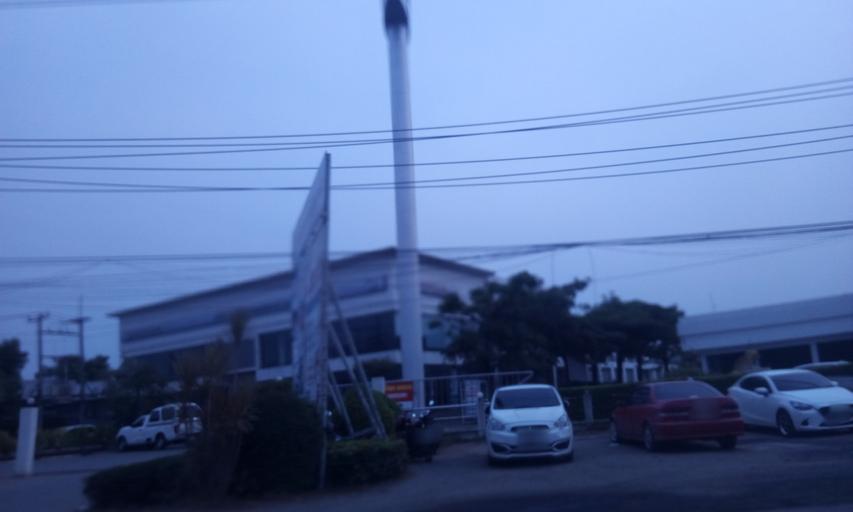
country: TH
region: Chachoengsao
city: Chachoengsao
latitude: 13.6591
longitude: 101.0565
